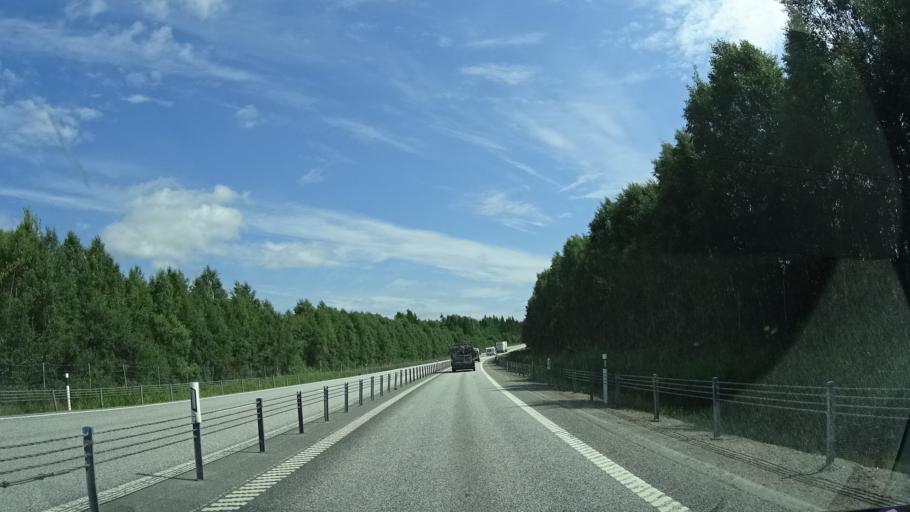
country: SE
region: OErebro
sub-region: Degerfors Kommun
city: Degerfors
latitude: 59.3255
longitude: 14.4255
